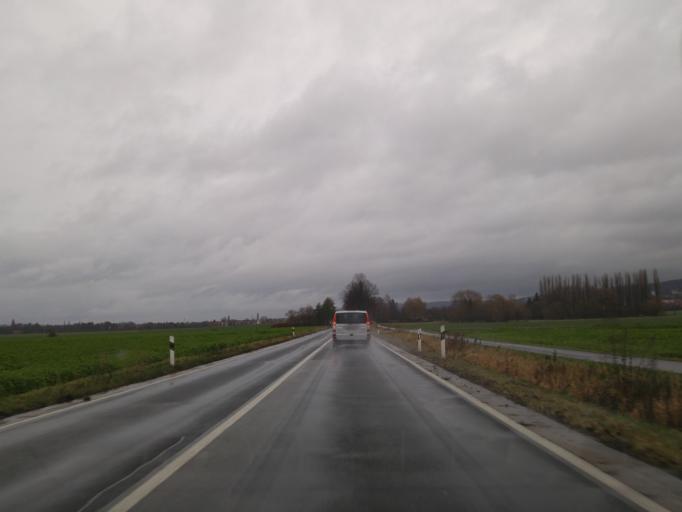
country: DE
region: Lower Saxony
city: Goettingen
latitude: 51.5002
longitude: 9.9373
